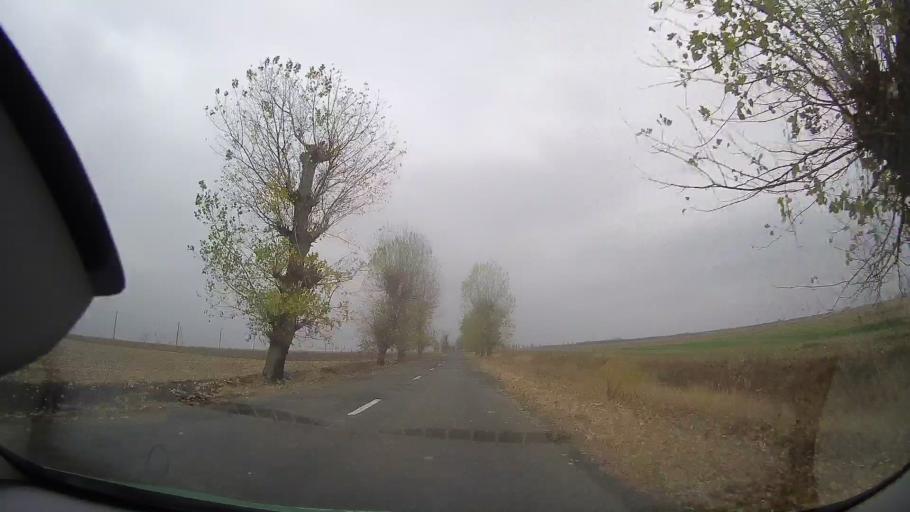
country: RO
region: Ialomita
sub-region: Comuna Grindu
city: Grindu
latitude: 44.7973
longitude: 26.8862
